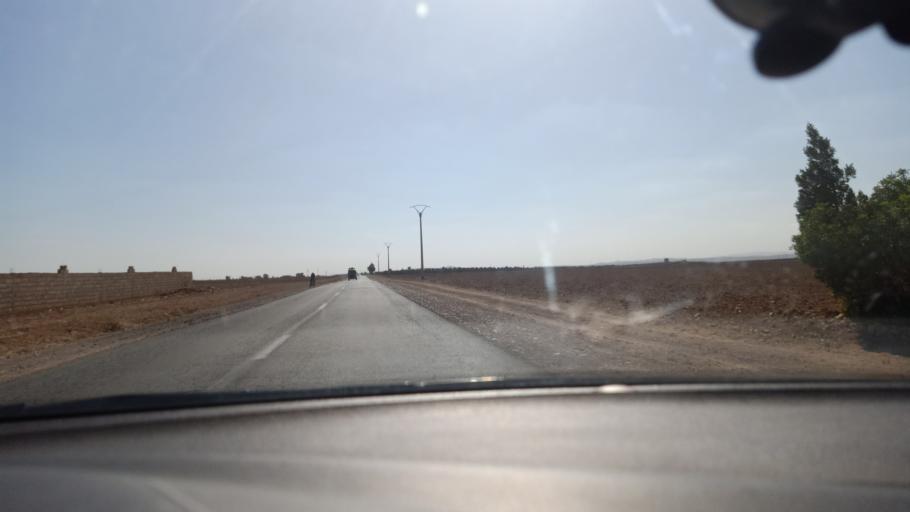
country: MA
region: Doukkala-Abda
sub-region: Safi
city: Youssoufia
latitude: 32.1280
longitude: -8.6007
